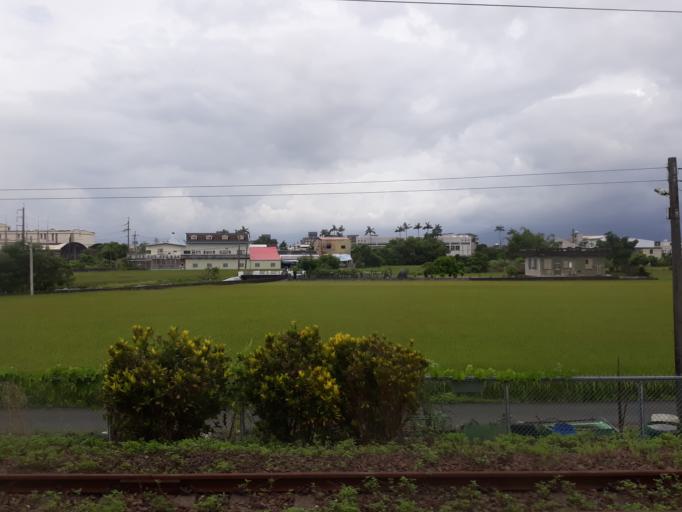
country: TW
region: Taiwan
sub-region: Yilan
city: Yilan
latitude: 24.6991
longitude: 121.7753
